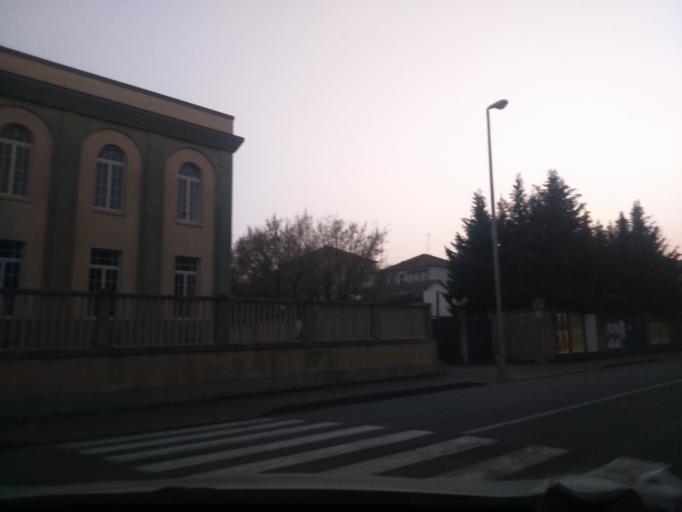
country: IT
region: Piedmont
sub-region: Provincia di Vercelli
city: Vercelli
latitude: 45.3197
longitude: 8.4180
